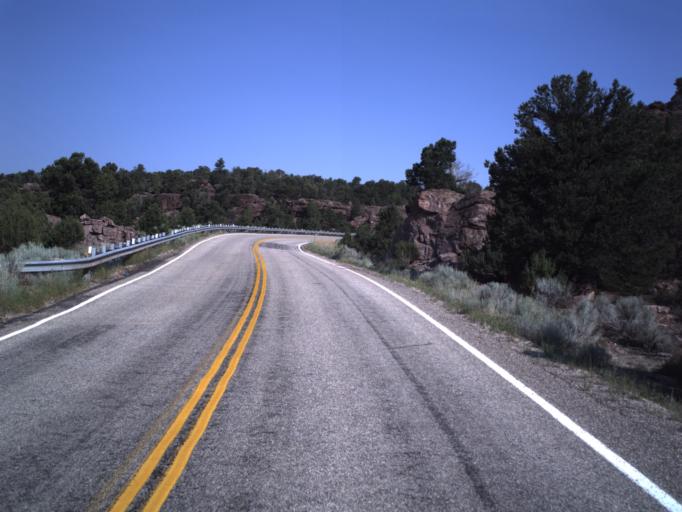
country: US
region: Utah
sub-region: Daggett County
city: Manila
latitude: 40.9212
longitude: -109.4162
